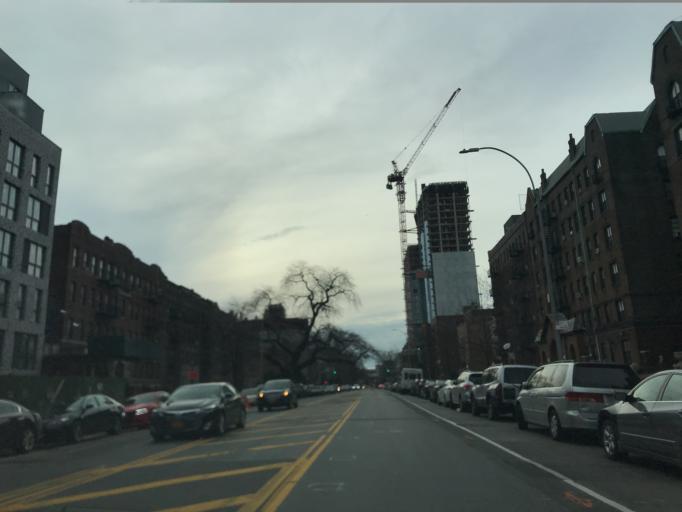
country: US
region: New York
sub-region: Kings County
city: Brooklyn
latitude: 40.6526
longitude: -73.9507
